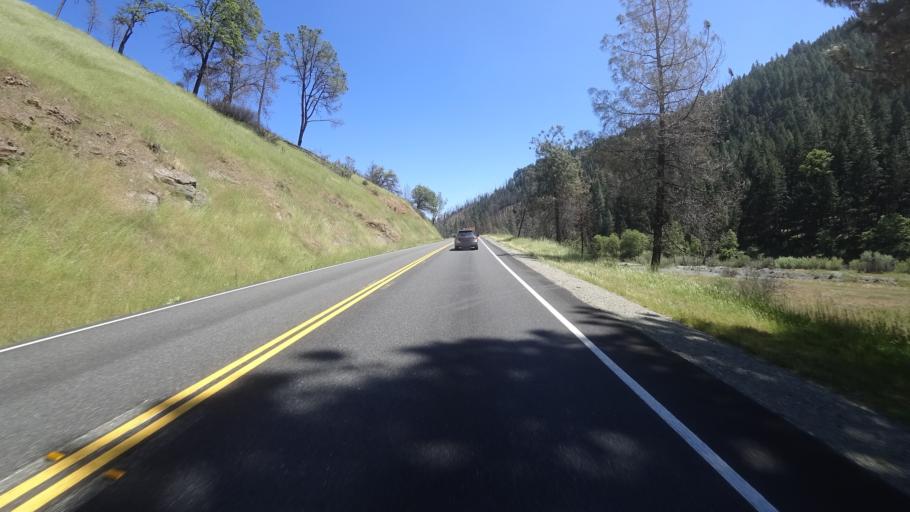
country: US
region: California
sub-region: Trinity County
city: Weaverville
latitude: 40.7672
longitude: -123.1180
